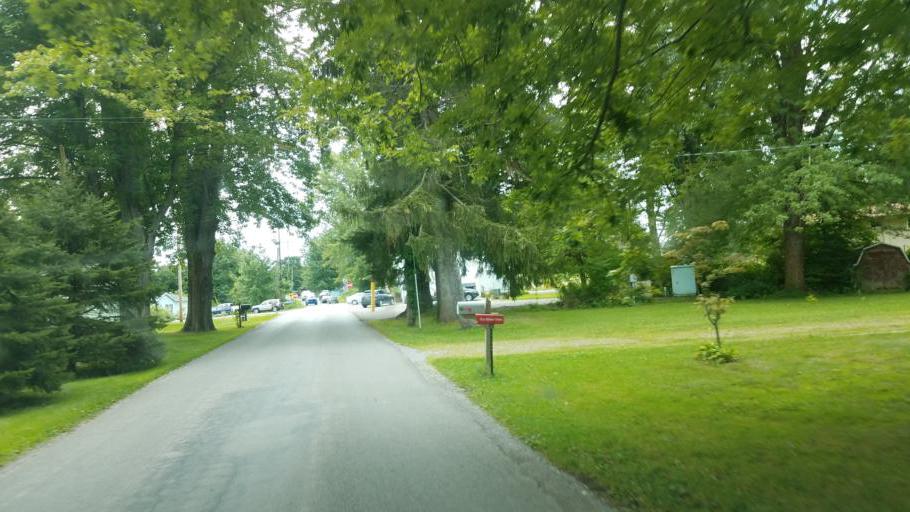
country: US
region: Pennsylvania
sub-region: Erie County
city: Lake City
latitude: 41.9954
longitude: -80.4264
